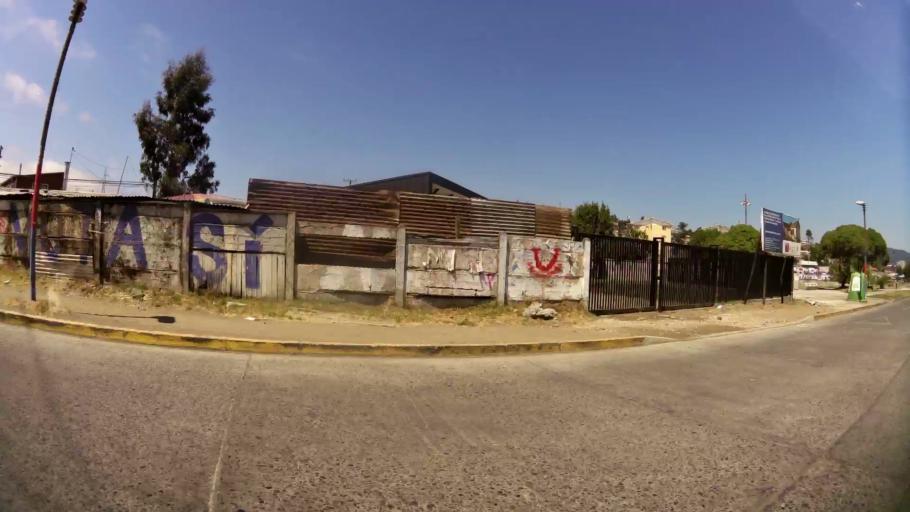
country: CL
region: Biobio
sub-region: Provincia de Concepcion
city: Concepcion
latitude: -36.8059
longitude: -73.0417
